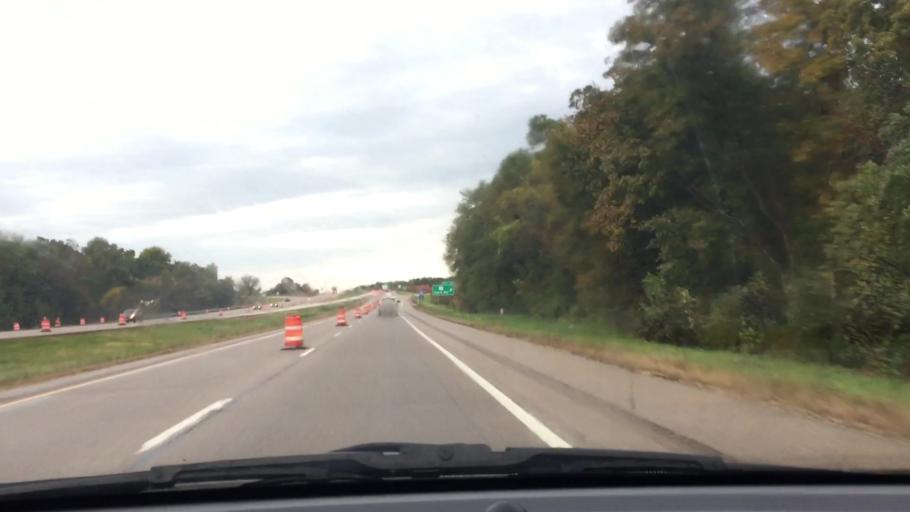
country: US
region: Wisconsin
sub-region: Rock County
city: Clinton
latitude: 42.5452
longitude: -88.9410
